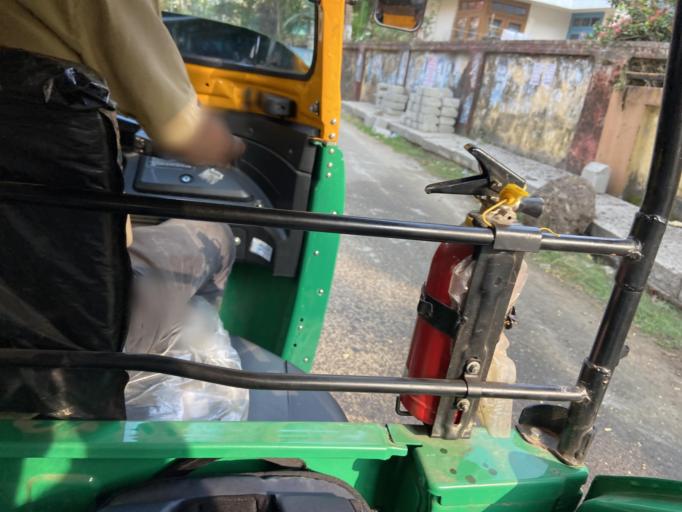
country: IN
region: Kerala
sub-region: Ernakulam
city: Cochin
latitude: 9.9593
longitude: 76.2494
